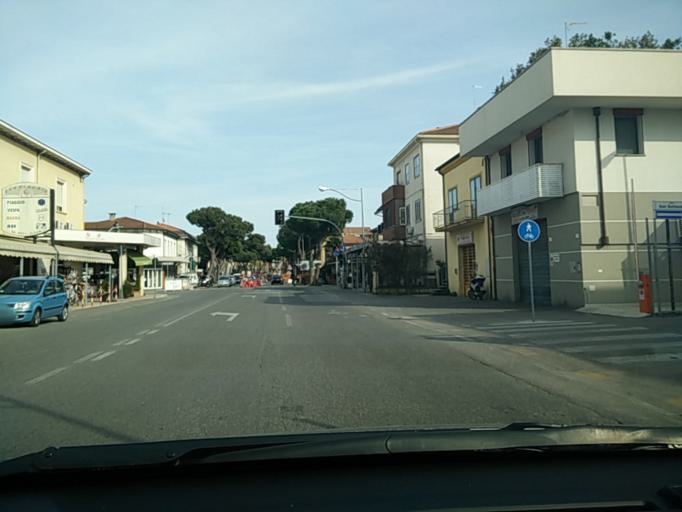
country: IT
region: Emilia-Romagna
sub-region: Provincia di Rimini
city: Rimini
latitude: 44.0670
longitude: 12.5578
